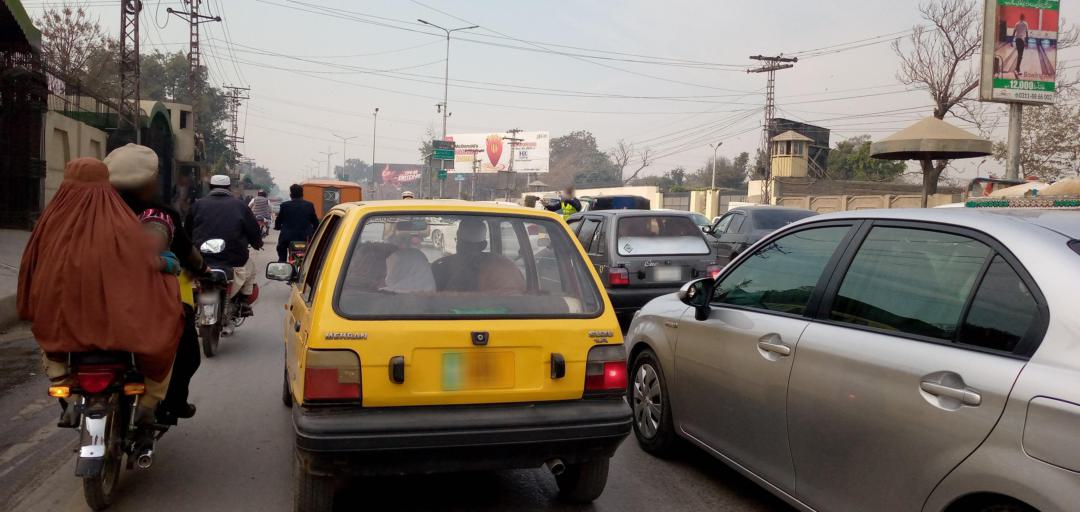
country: PK
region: Khyber Pakhtunkhwa
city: Peshawar
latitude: 34.0145
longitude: 71.5645
